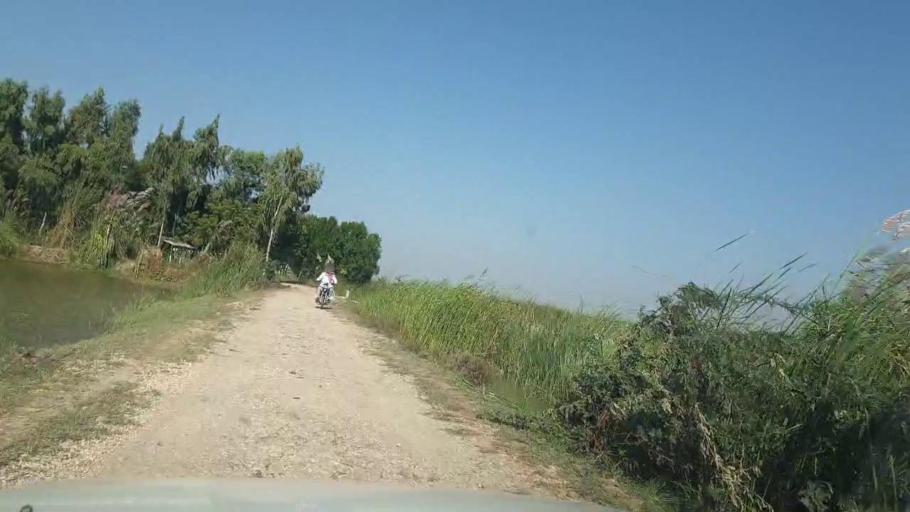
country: PK
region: Sindh
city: Chuhar Jamali
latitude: 24.4214
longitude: 67.8126
